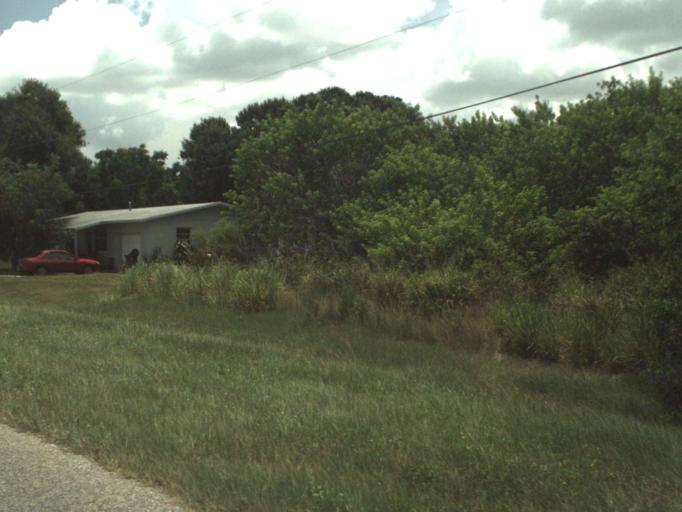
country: US
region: Florida
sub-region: Saint Lucie County
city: Fort Pierce South
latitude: 27.4068
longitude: -80.4286
